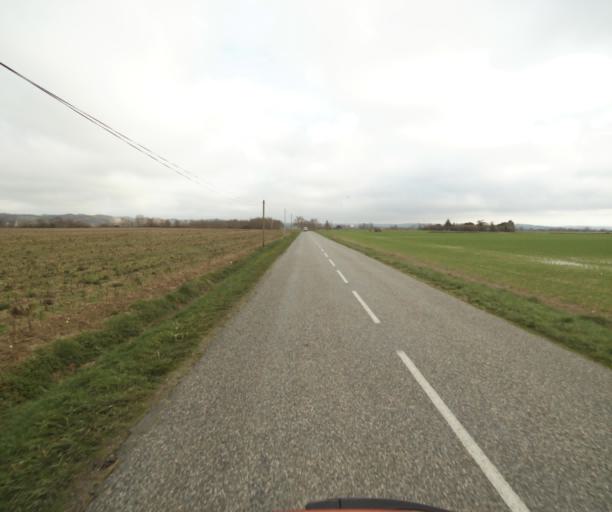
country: FR
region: Languedoc-Roussillon
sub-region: Departement de l'Aude
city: Belpech
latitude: 43.2157
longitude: 1.7181
